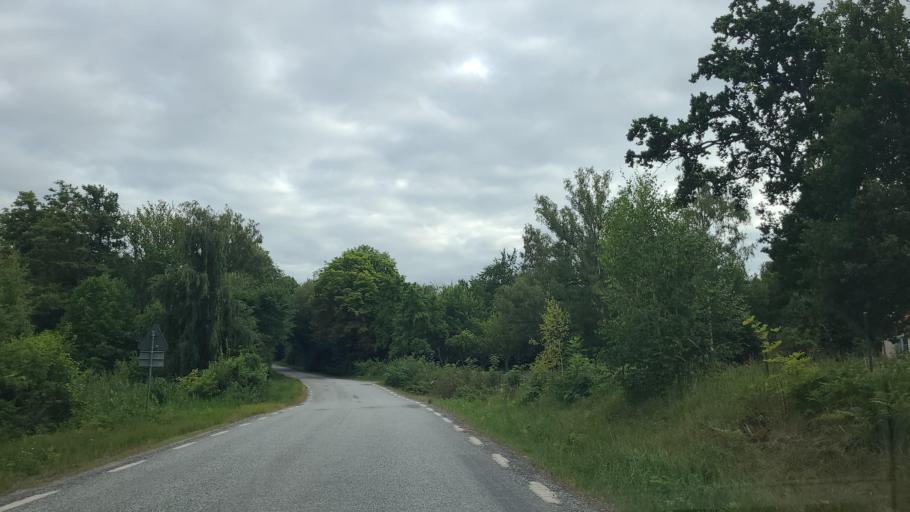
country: SE
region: Stockholm
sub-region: Upplands-Bro Kommun
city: Bro
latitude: 59.4909
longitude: 17.5677
